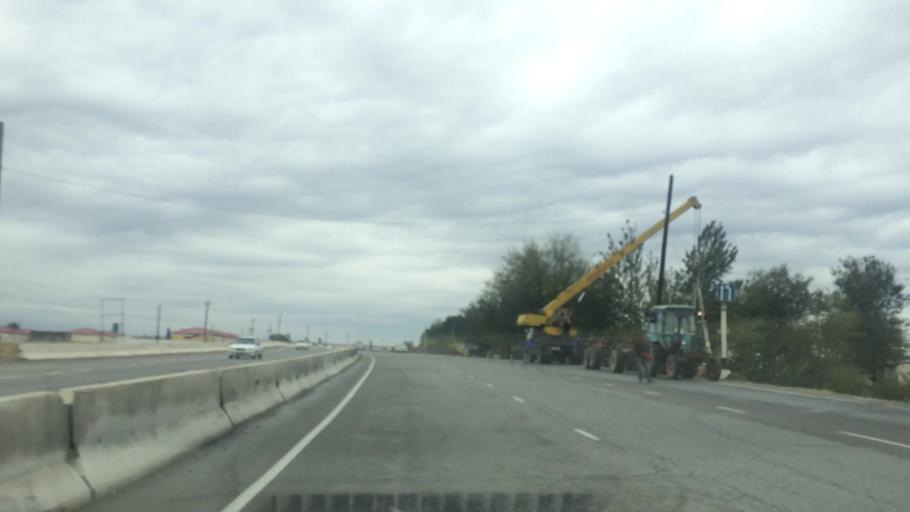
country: UZ
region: Jizzax
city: Jizzax
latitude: 39.9760
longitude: 67.5616
